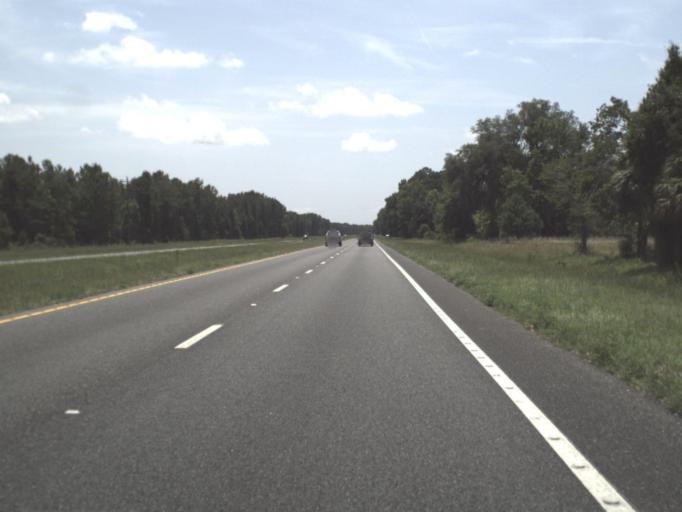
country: US
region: Florida
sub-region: Taylor County
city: Perry
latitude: 30.0041
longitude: -83.5119
